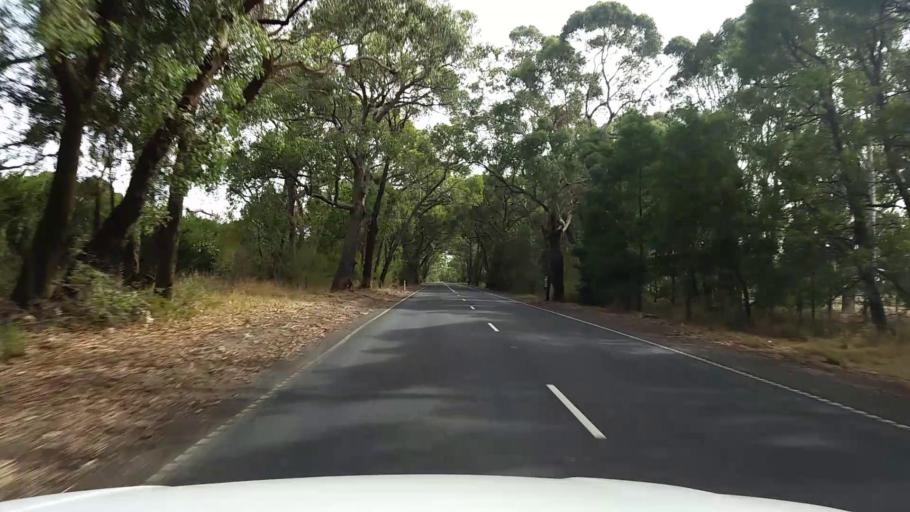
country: AU
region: Victoria
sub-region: Mornington Peninsula
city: Mount Martha
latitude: -38.3004
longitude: 145.0795
